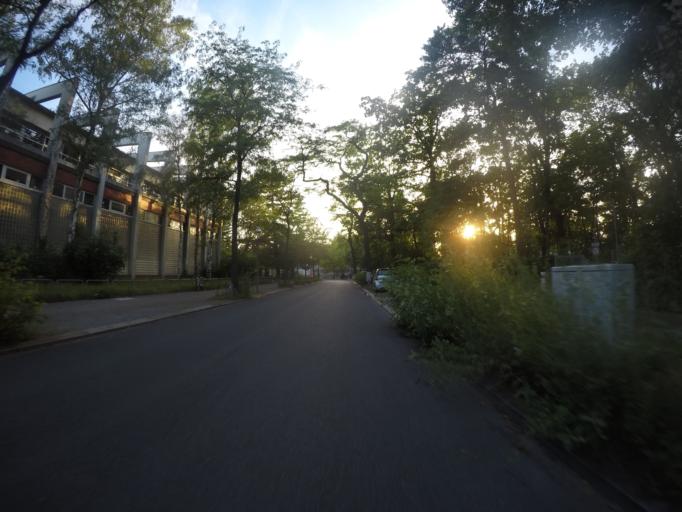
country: DE
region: Berlin
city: Halensee
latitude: 52.4920
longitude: 13.2819
